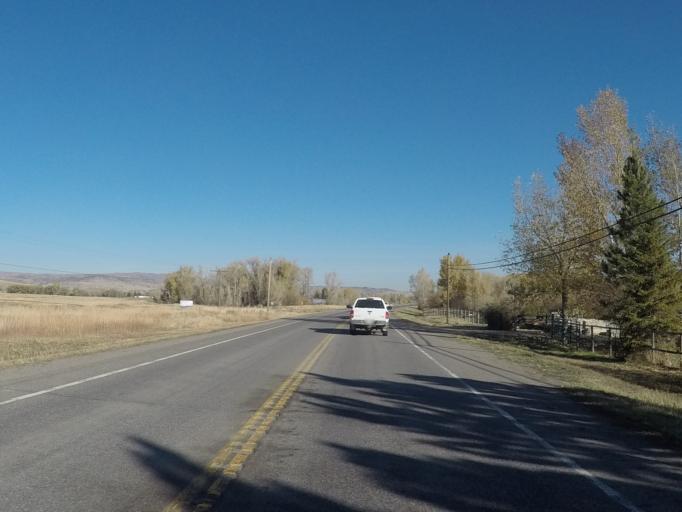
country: US
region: Montana
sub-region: Park County
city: Livingston
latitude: 45.6187
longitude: -110.5791
